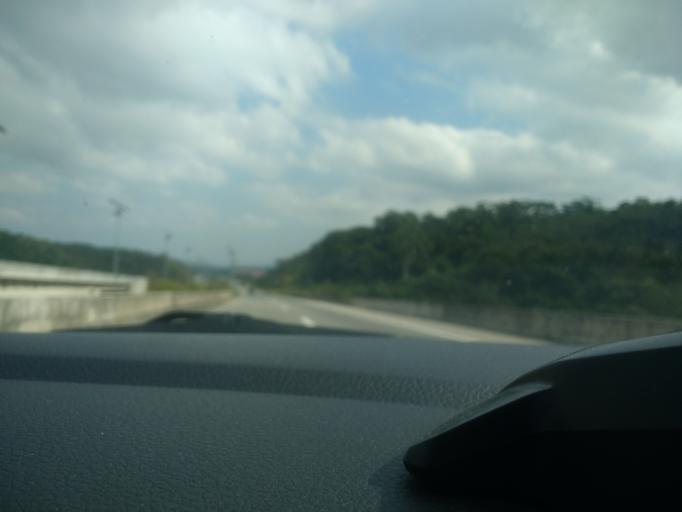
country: BR
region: Rio de Janeiro
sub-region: Queimados
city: Queimados
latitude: -22.6636
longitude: -43.5644
